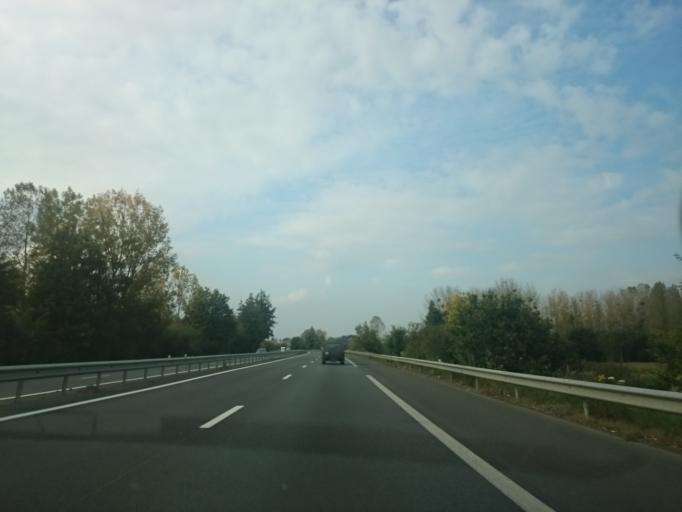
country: FR
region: Brittany
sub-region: Departement des Cotes-d'Armor
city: Broons
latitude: 48.3321
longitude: -2.2650
